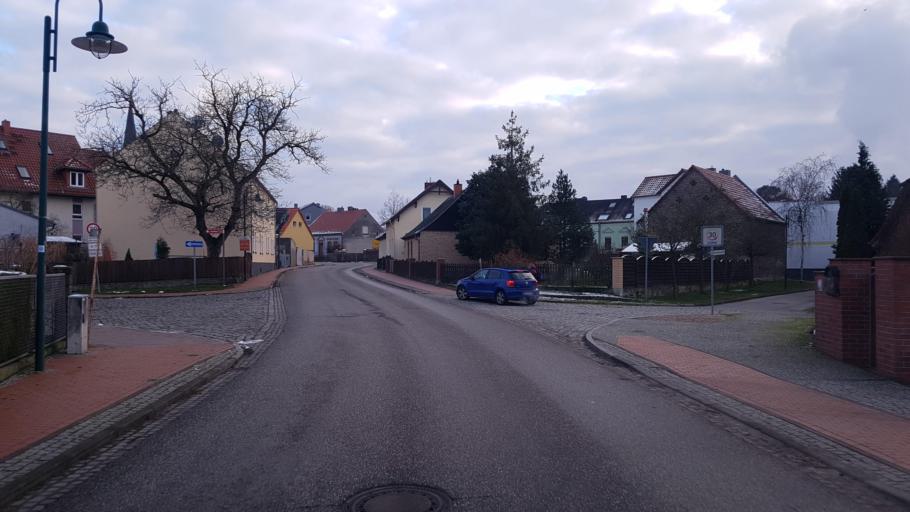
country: DE
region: Brandenburg
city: Rehfelde
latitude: 52.5084
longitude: 13.8449
